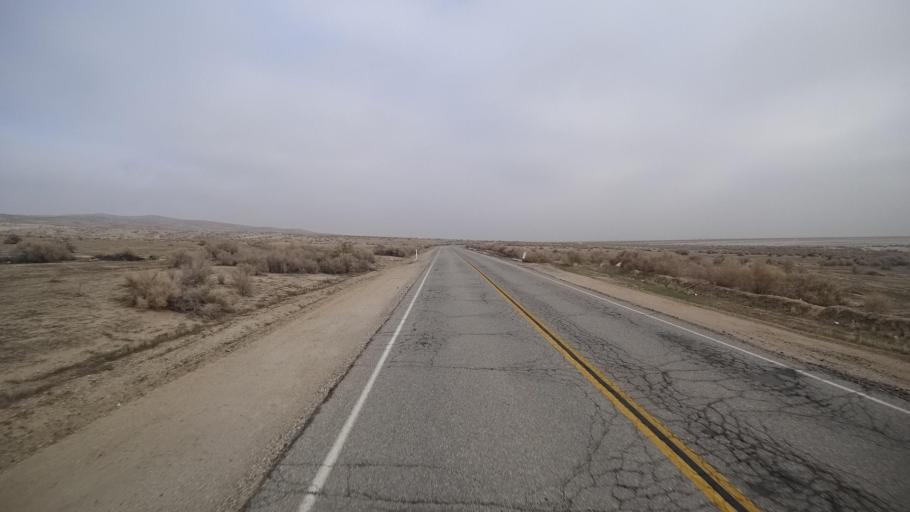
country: US
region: California
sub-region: Kern County
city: South Taft
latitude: 35.1321
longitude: -119.3999
